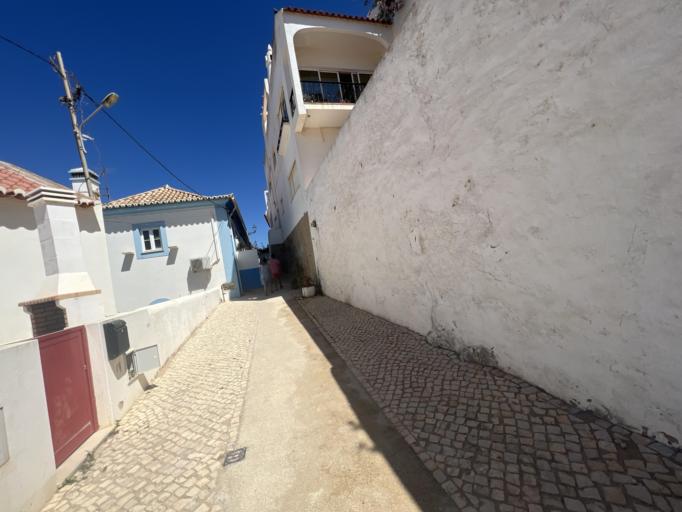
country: PT
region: Faro
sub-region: Portimao
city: Portimao
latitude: 37.1237
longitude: -8.5226
